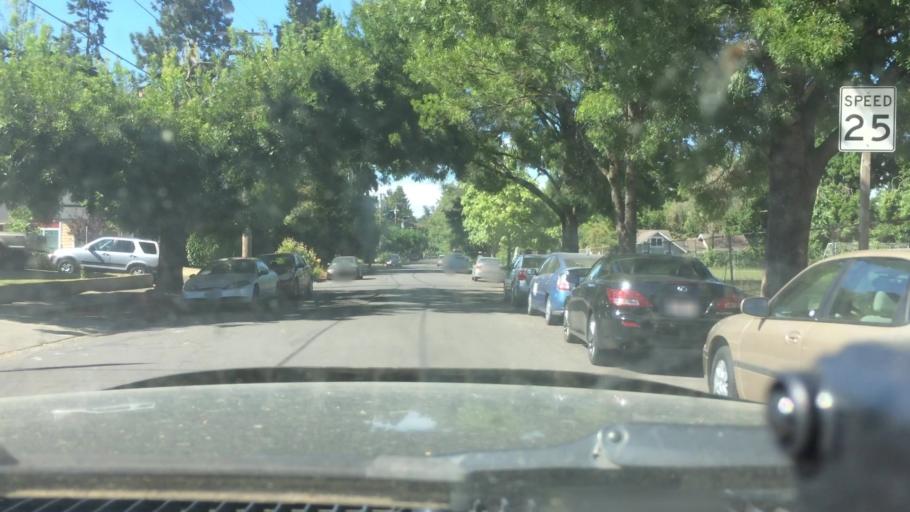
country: US
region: Oregon
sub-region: Lane County
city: Eugene
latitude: 44.0605
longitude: -123.1103
